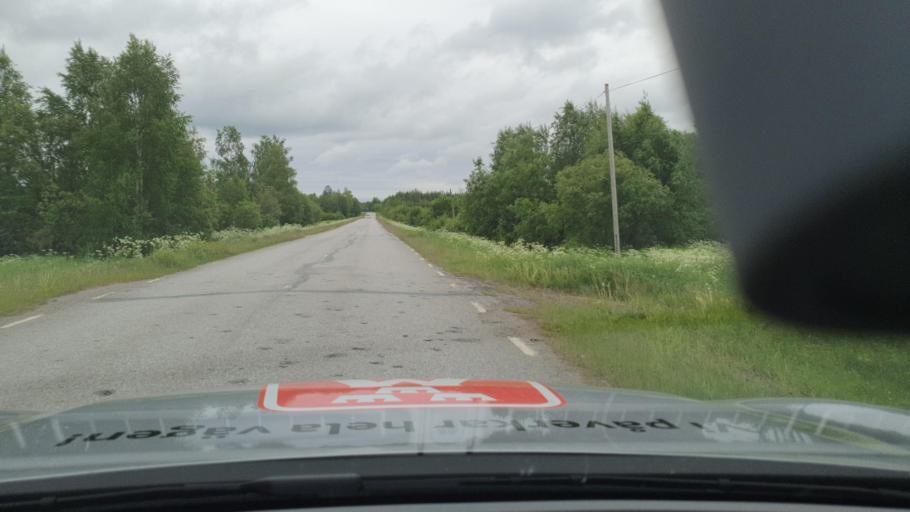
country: SE
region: Norrbotten
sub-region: Lulea Kommun
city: Ranea
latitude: 65.8473
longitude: 22.2512
